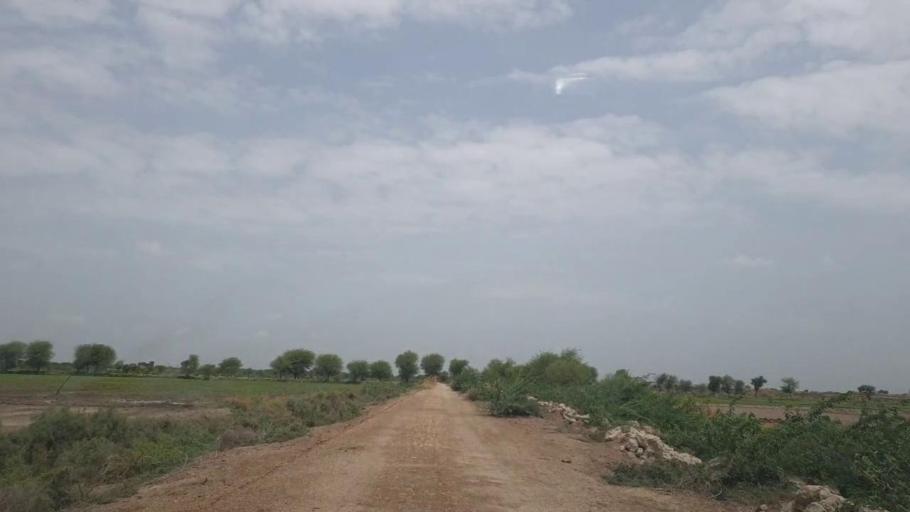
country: PK
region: Sindh
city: Tando Bago
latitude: 24.9244
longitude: 69.1003
